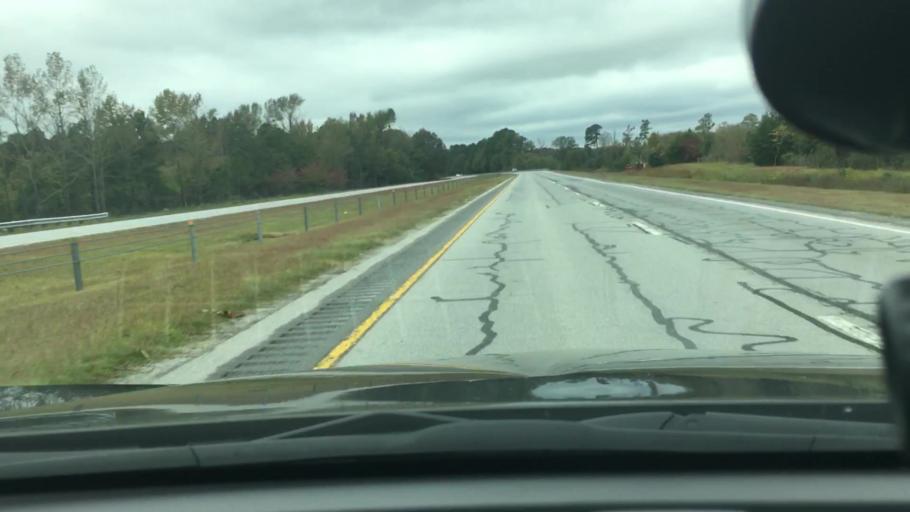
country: US
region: North Carolina
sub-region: Pitt County
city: Farmville
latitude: 35.6166
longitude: -77.6438
